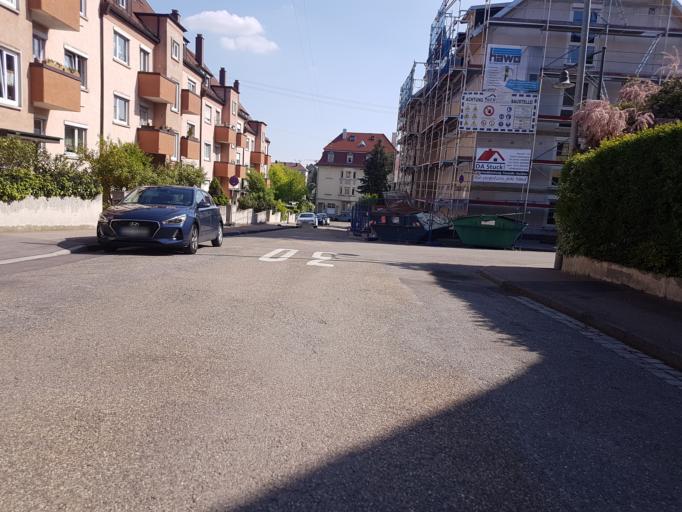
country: DE
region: Baden-Wuerttemberg
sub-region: Regierungsbezirk Stuttgart
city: Ludwigsburg
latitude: 48.8960
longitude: 9.1740
